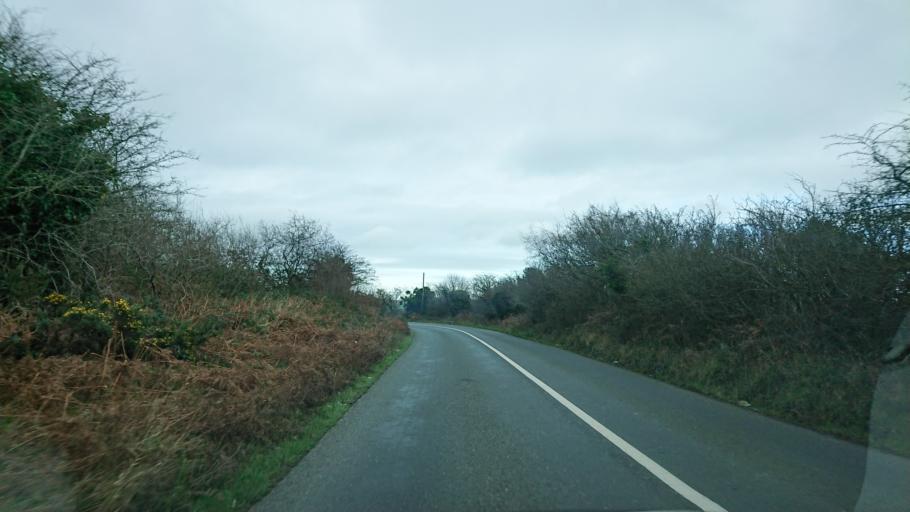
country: IE
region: Leinster
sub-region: Kilkenny
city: Mooncoin
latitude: 52.2139
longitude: -7.2428
